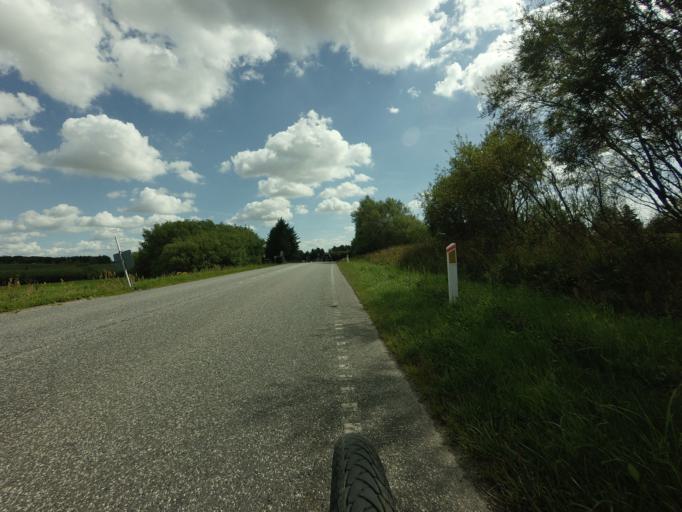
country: DK
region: North Denmark
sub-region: Hjorring Kommune
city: Hjorring
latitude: 57.4529
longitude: 9.9169
